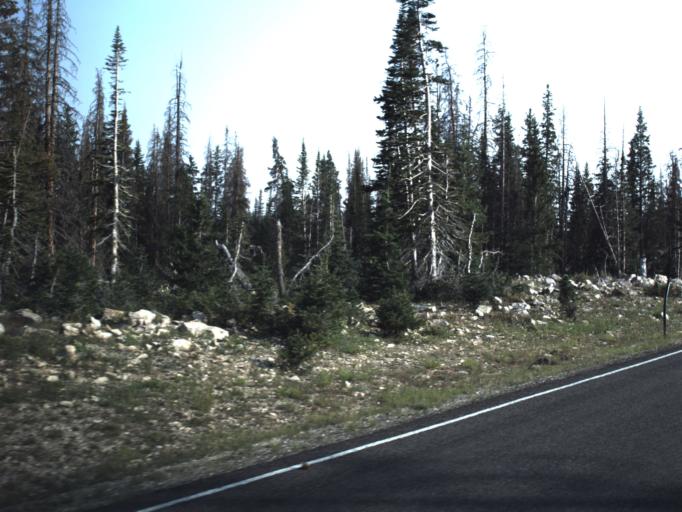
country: US
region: Utah
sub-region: Summit County
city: Kamas
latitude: 40.7260
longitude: -110.8644
